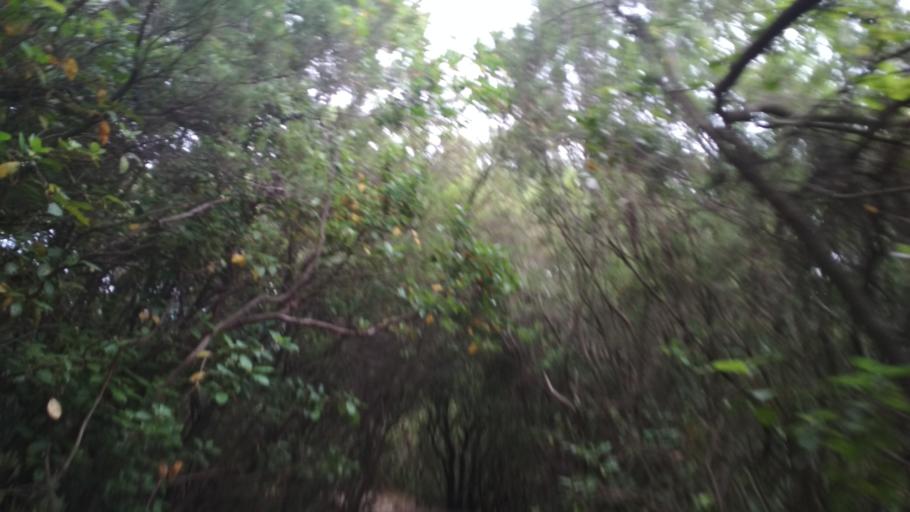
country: ES
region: Catalonia
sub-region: Provincia de Barcelona
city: Horta-Guinardo
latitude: 41.4453
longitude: 2.1329
